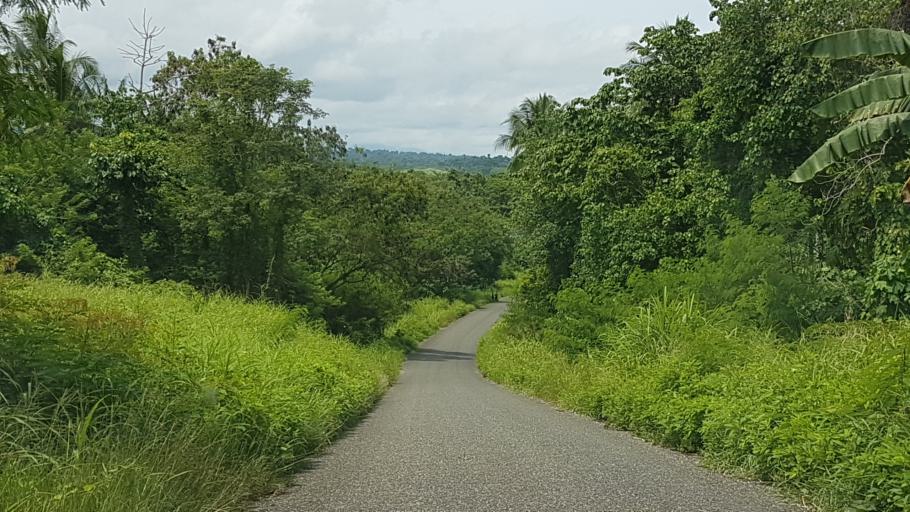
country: PG
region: Madang
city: Madang
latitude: -4.5903
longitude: 145.5386
